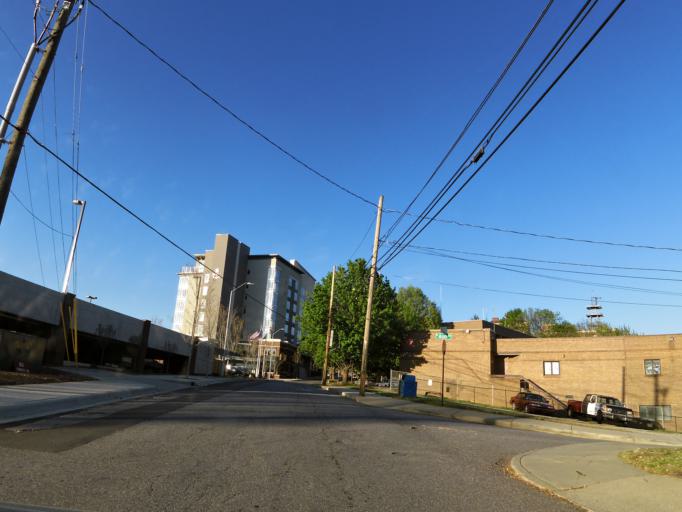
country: US
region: North Carolina
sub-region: Buncombe County
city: Asheville
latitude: 35.5952
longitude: -82.5607
